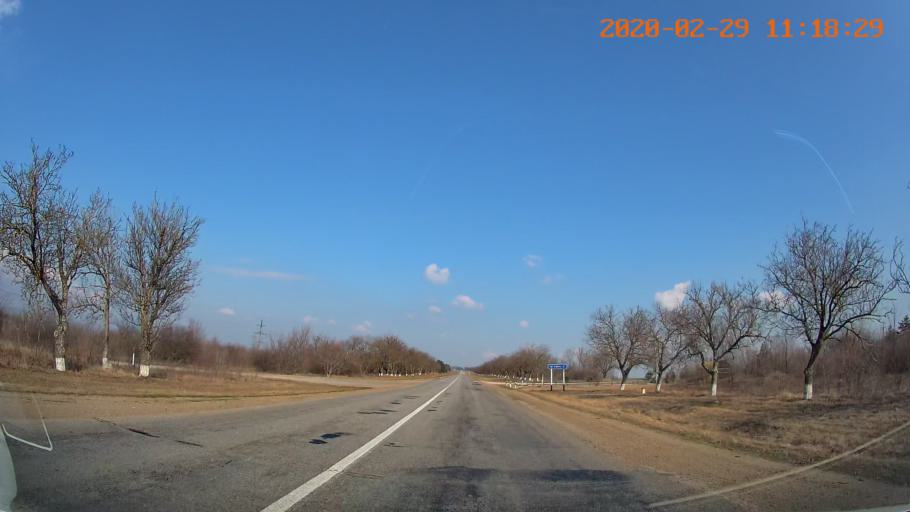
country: MD
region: Telenesti
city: Cocieri
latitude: 47.3355
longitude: 29.1735
